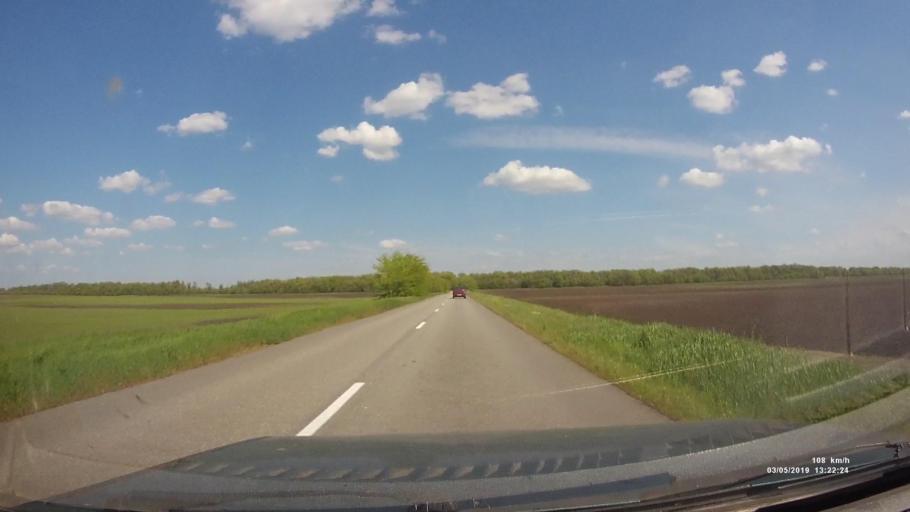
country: RU
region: Rostov
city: Semikarakorsk
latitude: 47.5609
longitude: 40.7613
